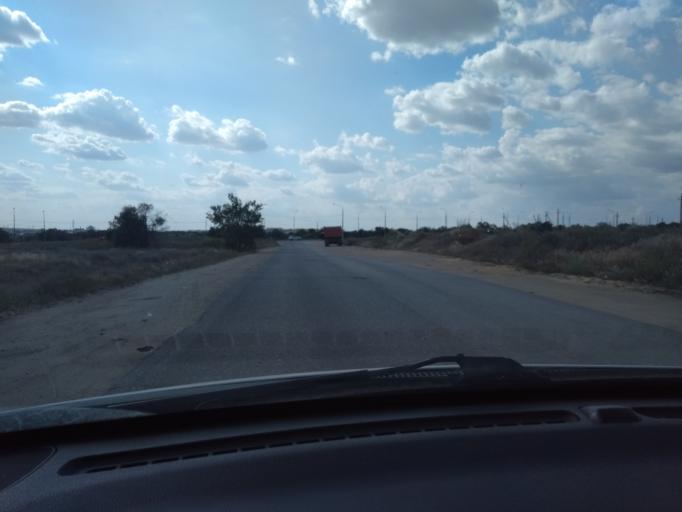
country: RU
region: Volgograd
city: Vodstroy
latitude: 48.8066
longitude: 44.5254
